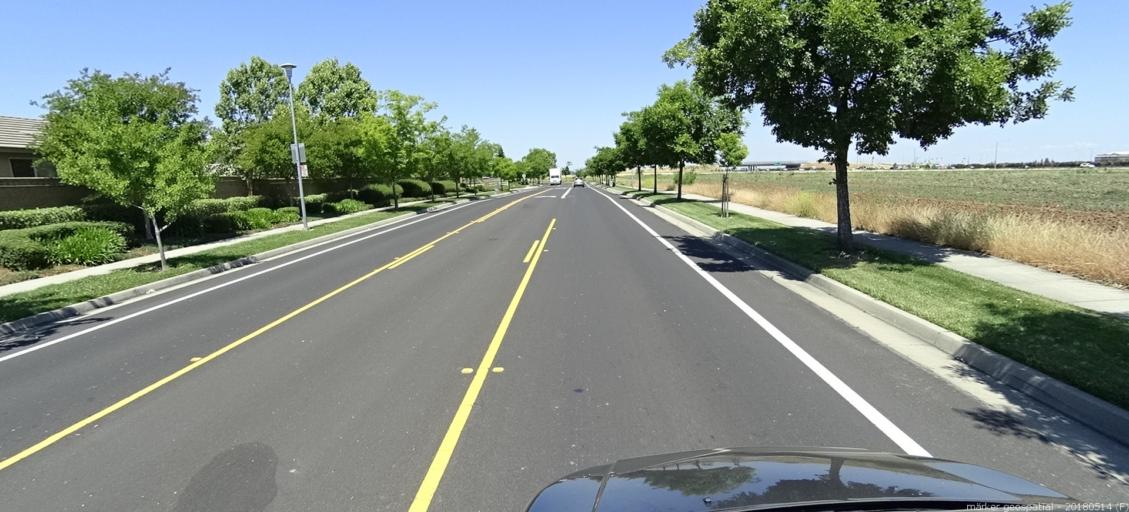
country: US
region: California
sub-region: Yolo County
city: West Sacramento
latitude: 38.6371
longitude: -121.5254
